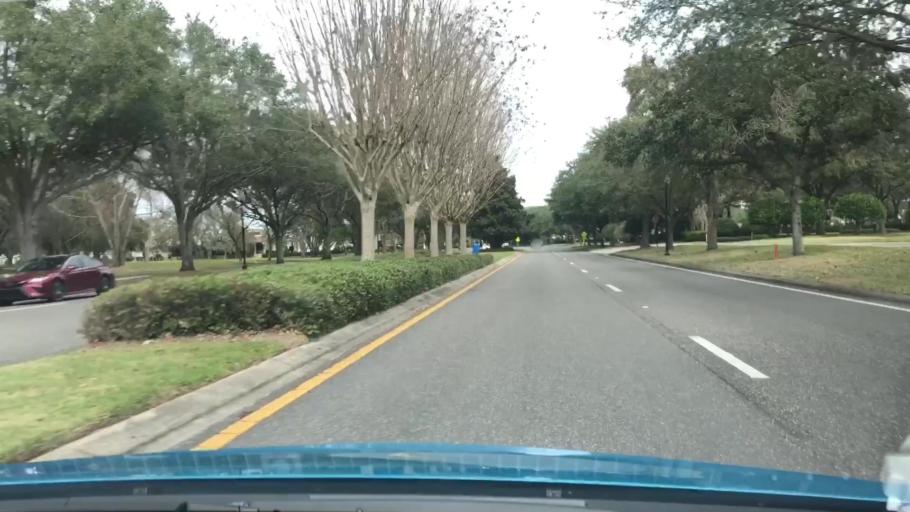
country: US
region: Florida
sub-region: Seminole County
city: Heathrow
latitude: 28.7767
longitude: -81.3583
